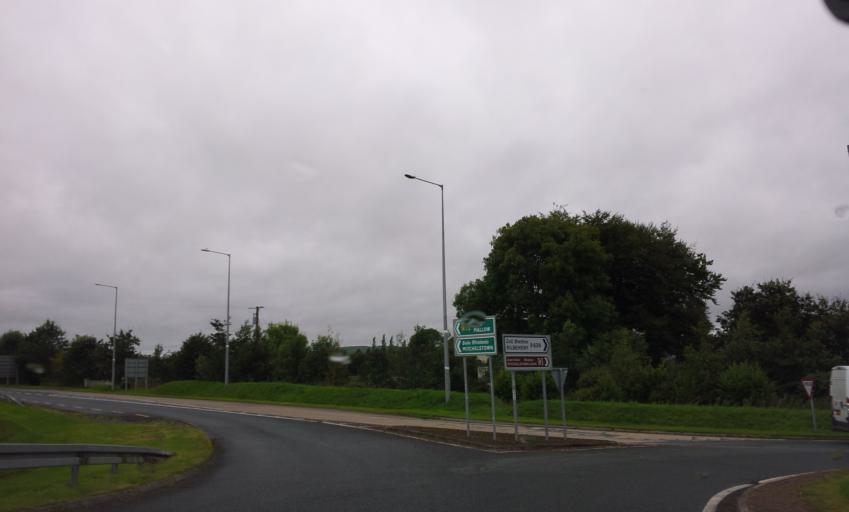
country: IE
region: Munster
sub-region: County Cork
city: Mitchelstown
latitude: 52.2862
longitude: -8.2191
